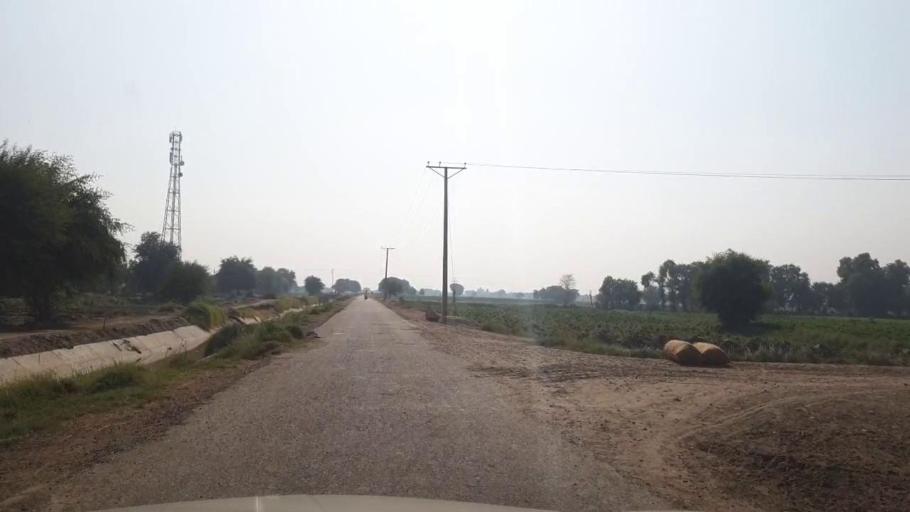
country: PK
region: Sindh
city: Bhan
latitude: 26.5292
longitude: 67.7781
